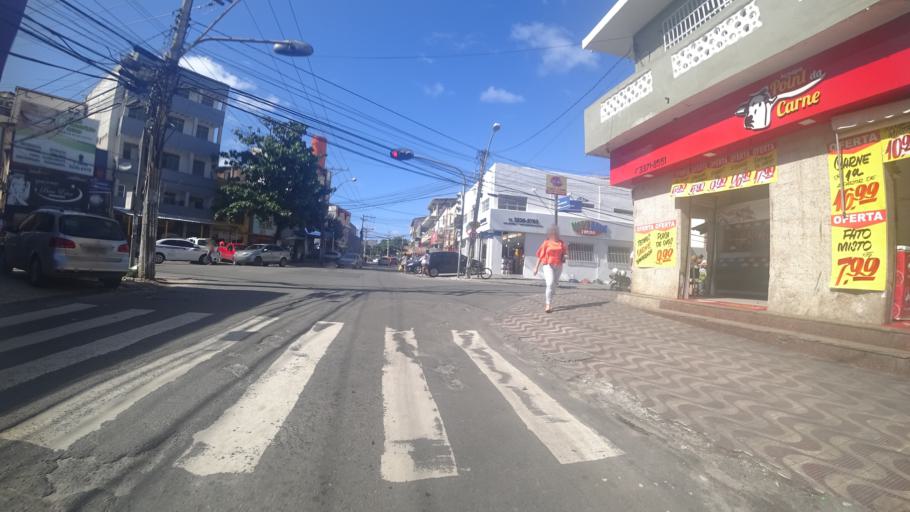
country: BR
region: Bahia
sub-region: Salvador
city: Salvador
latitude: -12.9772
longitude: -38.4300
